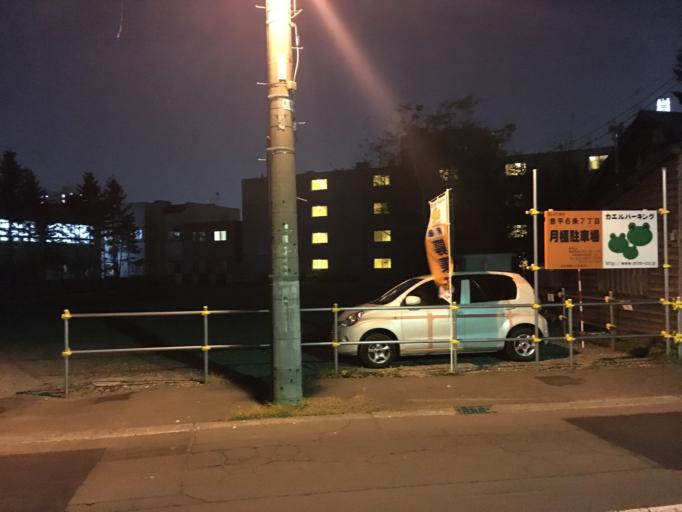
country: JP
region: Hokkaido
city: Sapporo
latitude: 43.0474
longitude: 141.3710
